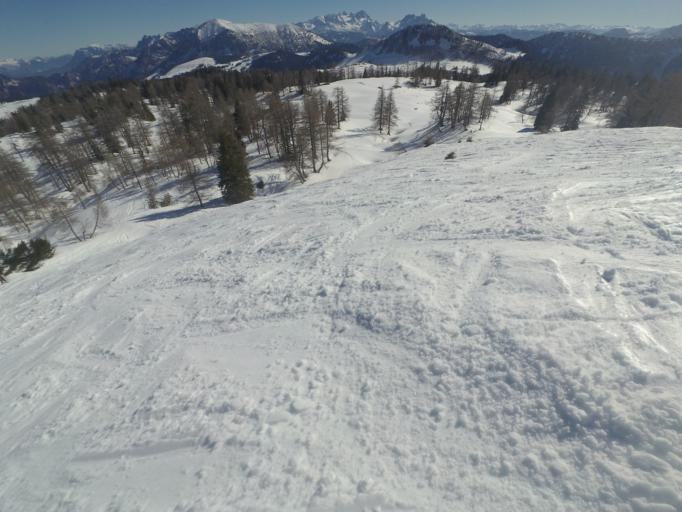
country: AT
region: Upper Austria
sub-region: Politischer Bezirk Gmunden
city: Sankt Wolfgang im Salzkammergut
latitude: 47.6657
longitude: 13.3784
